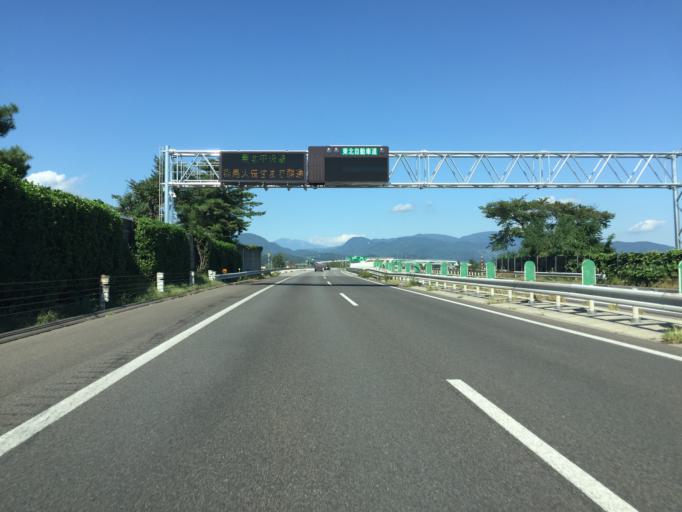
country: JP
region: Fukushima
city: Fukushima-shi
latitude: 37.7815
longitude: 140.4137
